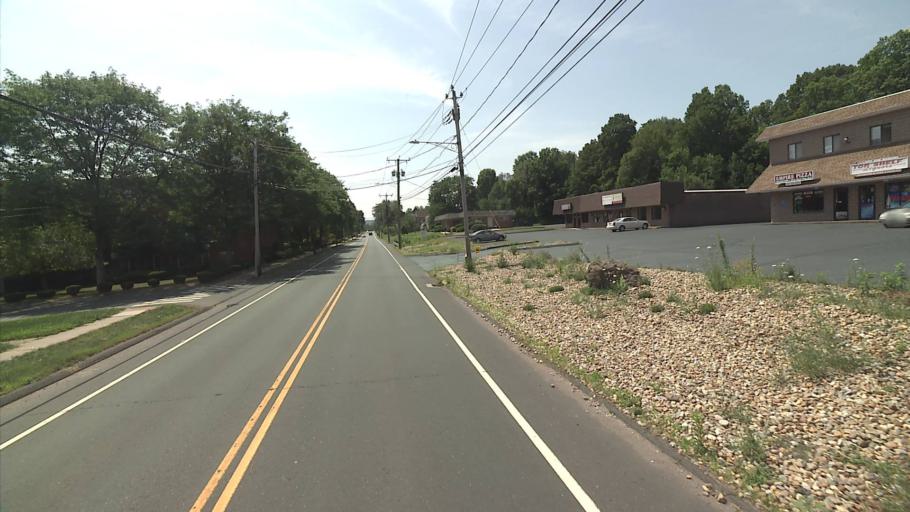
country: US
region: Connecticut
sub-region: Hartford County
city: Kensington
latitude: 41.6406
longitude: -72.7699
